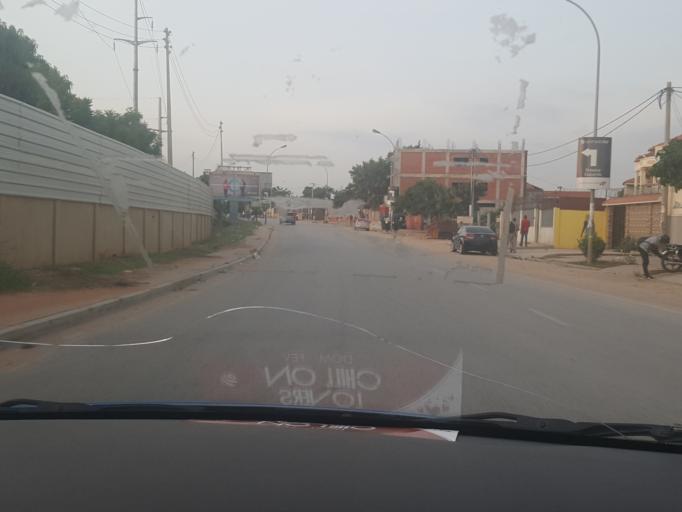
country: AO
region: Luanda
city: Luanda
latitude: -8.9134
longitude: 13.2019
